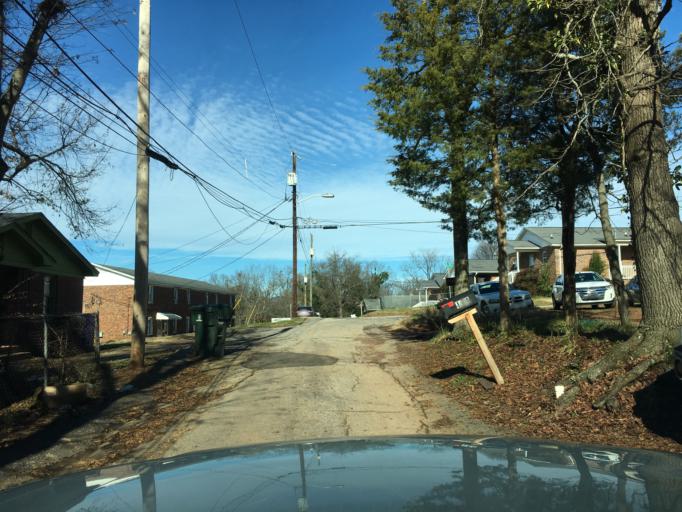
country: US
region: South Carolina
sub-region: Greenville County
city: Greenville
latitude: 34.8589
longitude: -82.3818
